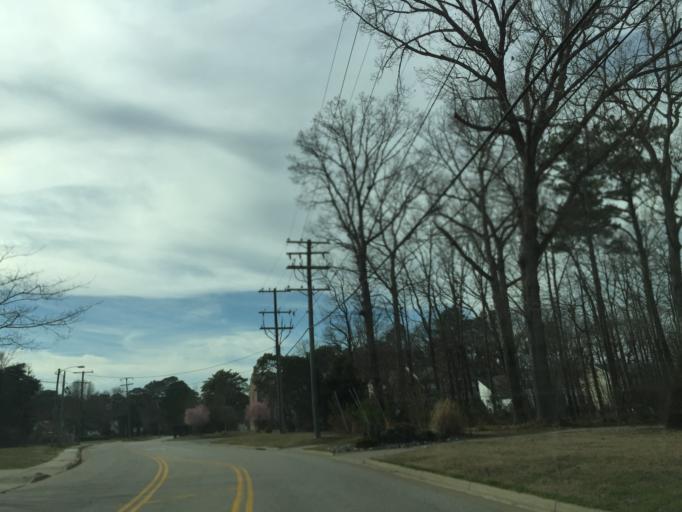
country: US
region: Virginia
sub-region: City of Newport News
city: Newport News
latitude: 37.0765
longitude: -76.5067
